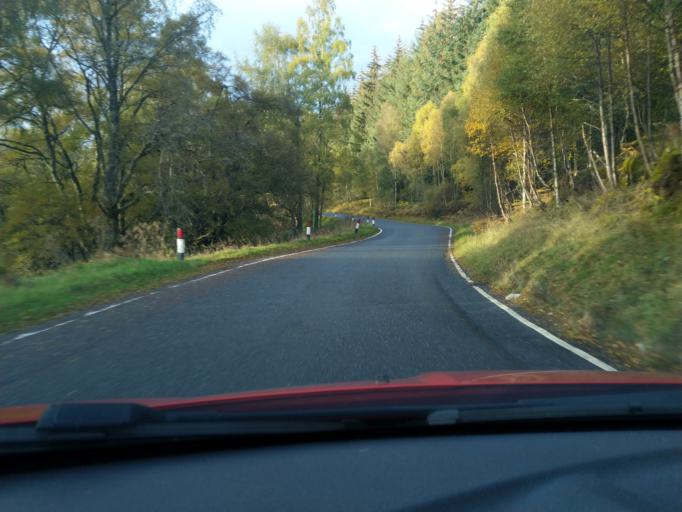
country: GB
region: Scotland
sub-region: Perth and Kinross
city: Aberfeldy
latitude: 56.7181
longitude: -4.1172
